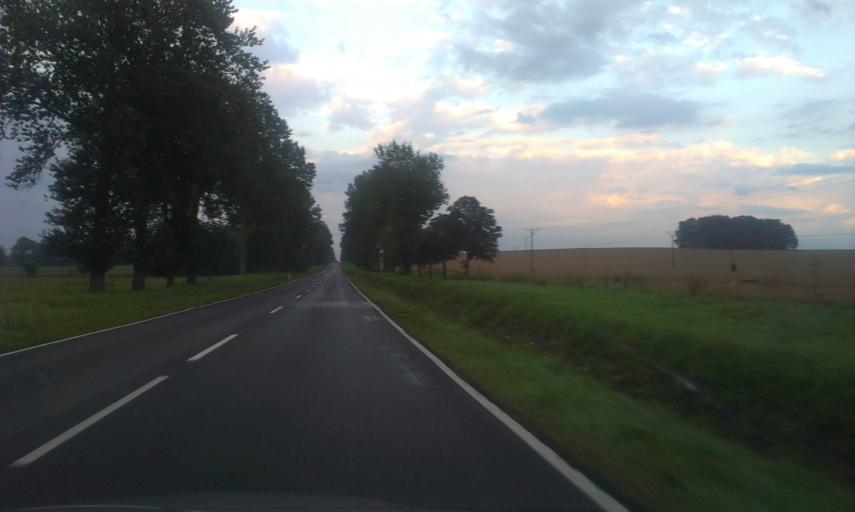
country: PL
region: West Pomeranian Voivodeship
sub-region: Powiat koszalinski
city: Sianow
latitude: 54.1445
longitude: 16.2516
